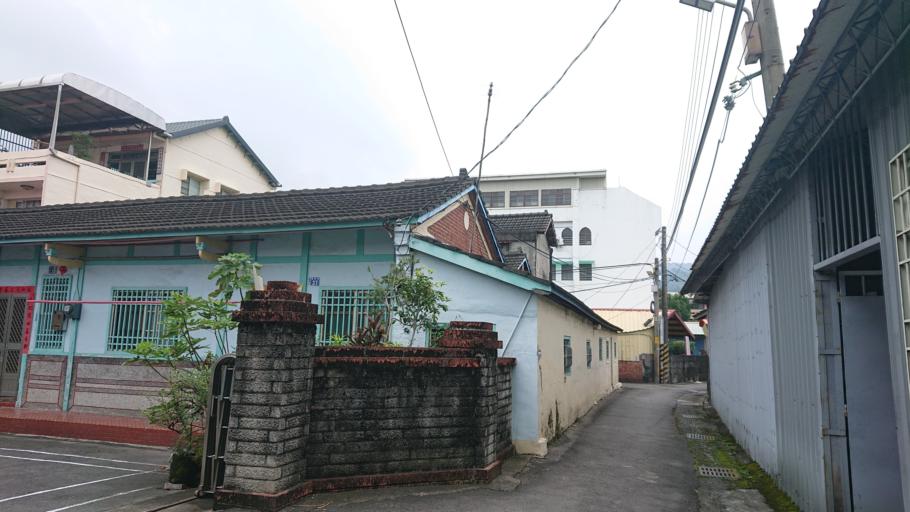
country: TW
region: Taiwan
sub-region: Nantou
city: Nantou
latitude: 23.8092
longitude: 120.6175
